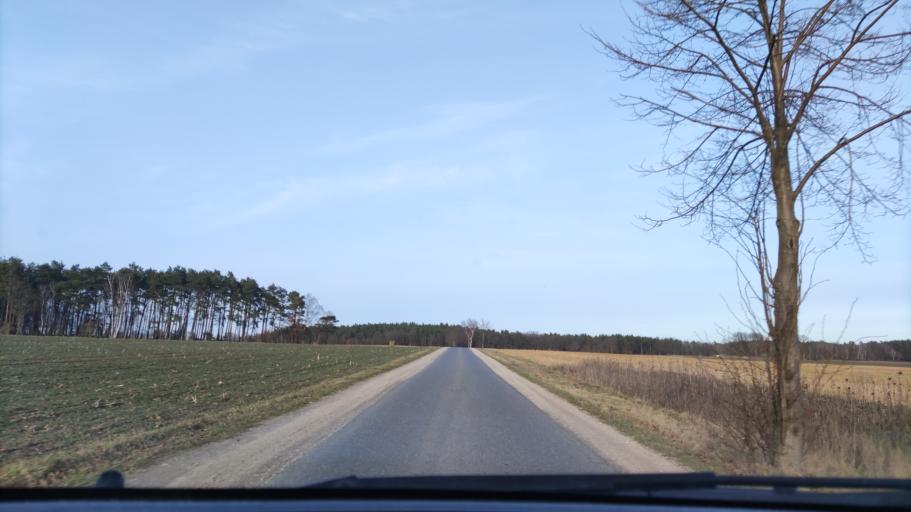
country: DE
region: Lower Saxony
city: Dahlenburg
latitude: 53.1992
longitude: 10.7005
